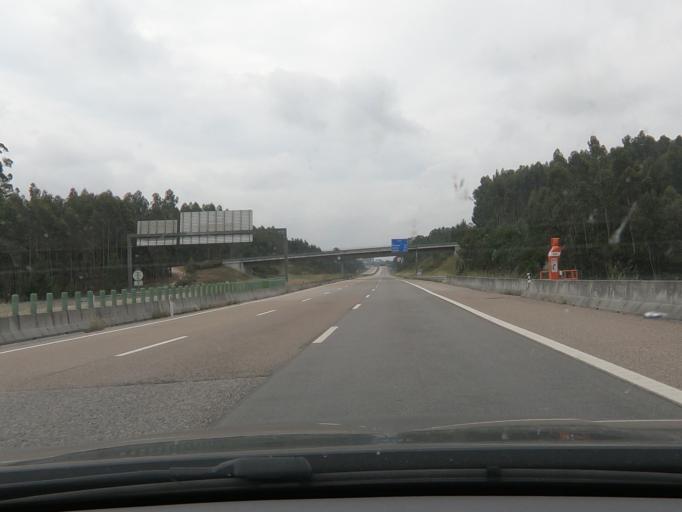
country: PT
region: Coimbra
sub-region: Figueira da Foz
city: Lavos
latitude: 40.0391
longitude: -8.8134
